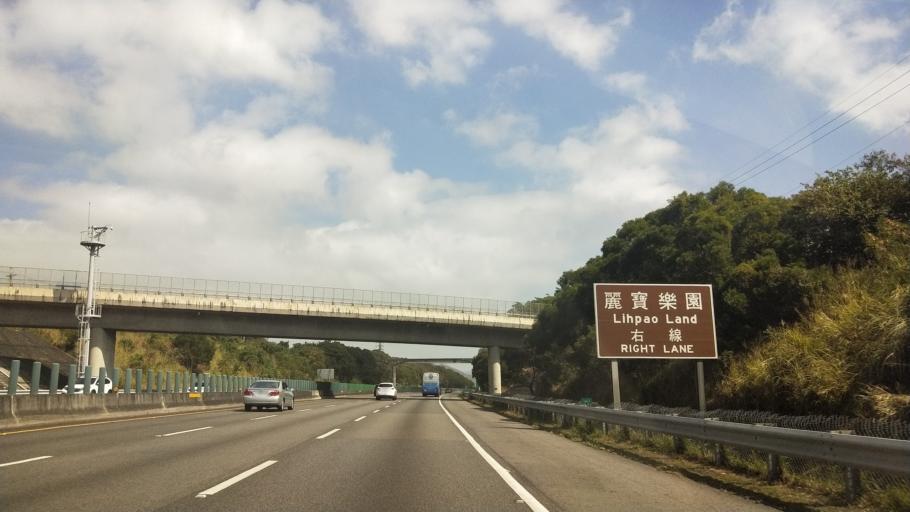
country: TW
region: Taiwan
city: Fengyuan
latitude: 24.3291
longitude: 120.6272
